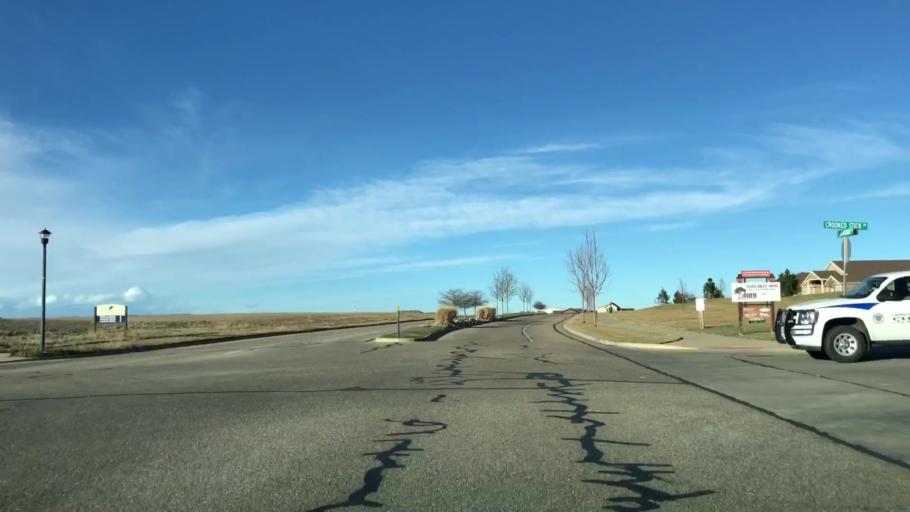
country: US
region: Colorado
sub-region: Weld County
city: Windsor
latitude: 40.4507
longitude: -104.9770
